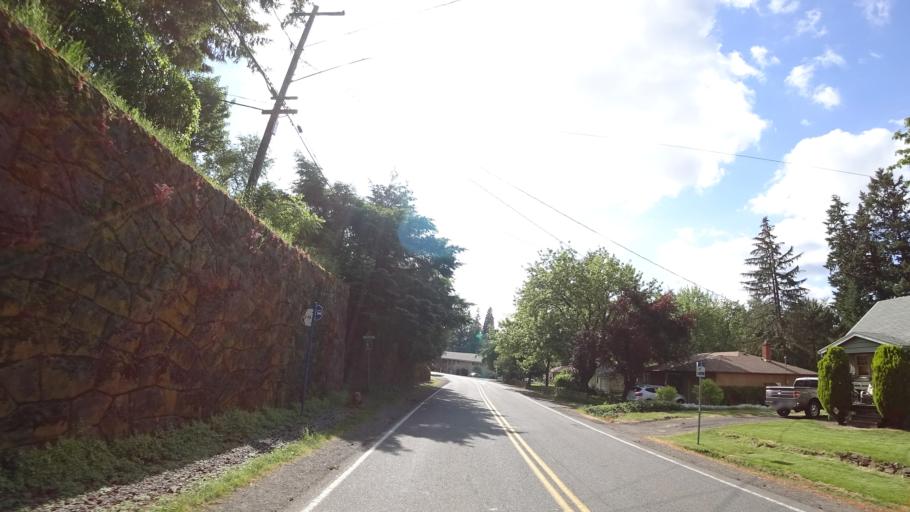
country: US
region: Oregon
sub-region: Washington County
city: Garden Home-Whitford
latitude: 45.4663
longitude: -122.7205
